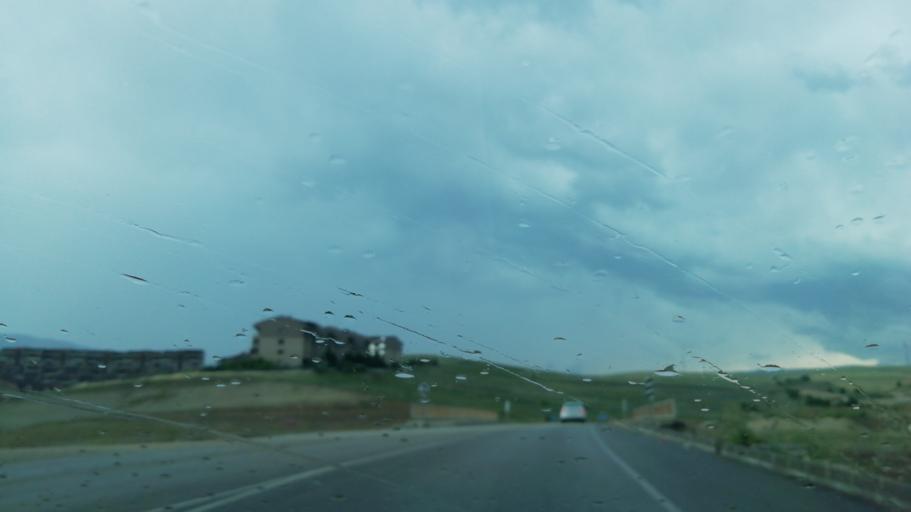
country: TR
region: Karabuk
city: Safranbolu
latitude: 41.2236
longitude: 32.7224
